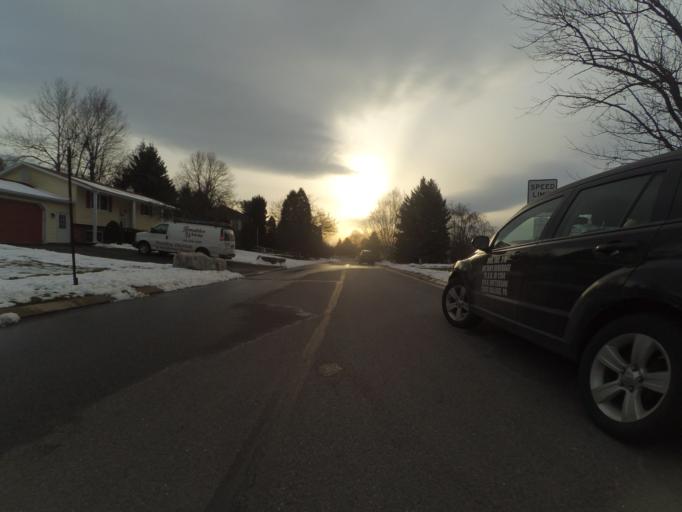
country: US
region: Pennsylvania
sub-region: Centre County
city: Lemont
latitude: 40.8184
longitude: -77.8137
